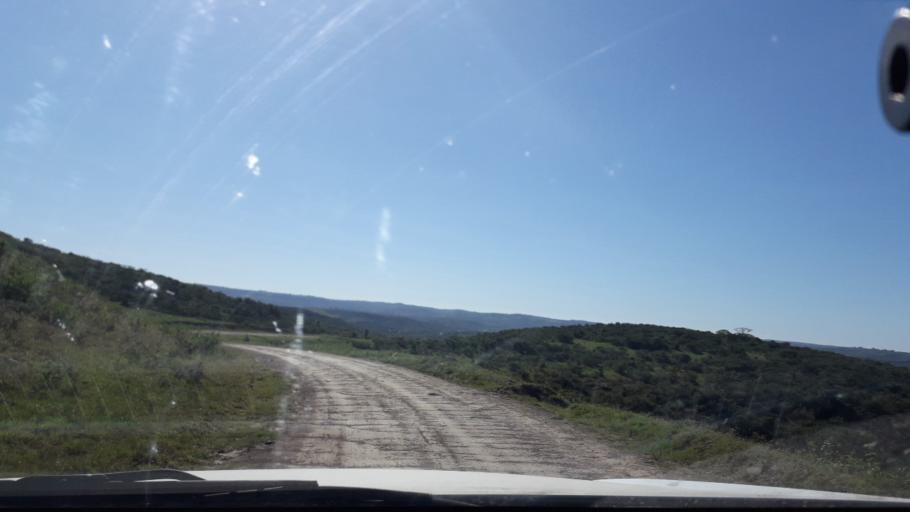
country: ZA
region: Eastern Cape
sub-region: Amathole District Municipality
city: Komga
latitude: -32.7836
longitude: 27.9567
